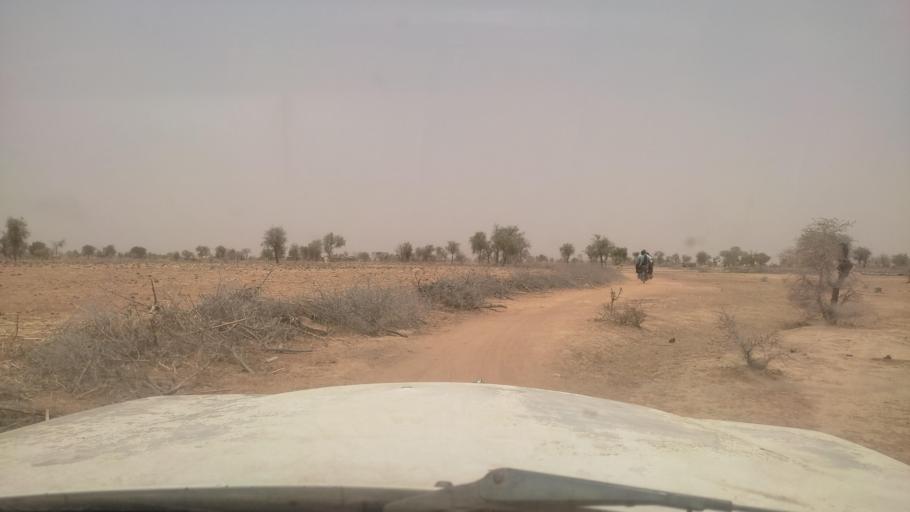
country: BF
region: Est
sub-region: Gnagna Province
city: Bogande
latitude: 13.0393
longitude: -0.0698
